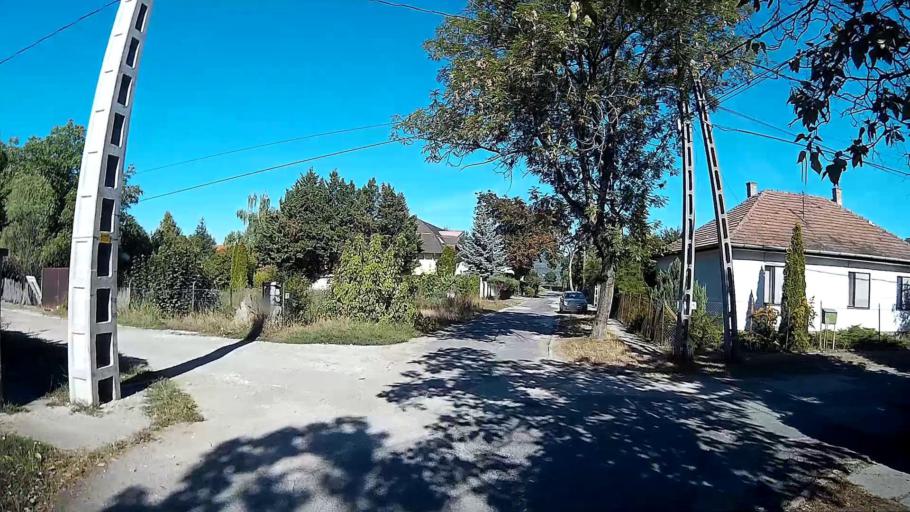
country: HU
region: Pest
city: Szentendre
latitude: 47.6511
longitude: 19.0661
